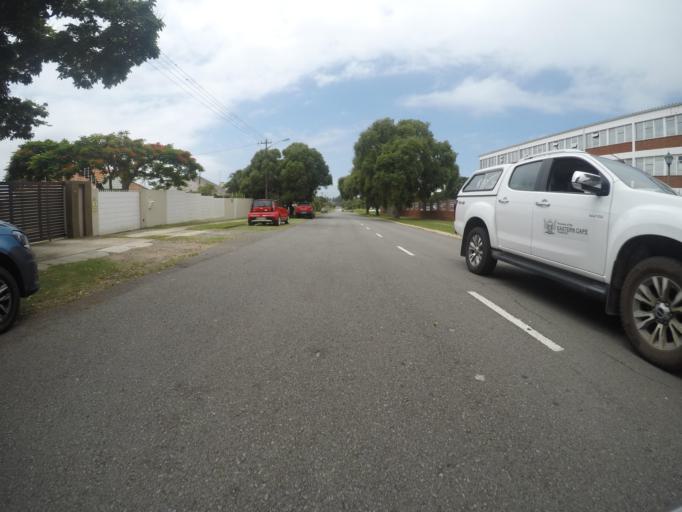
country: ZA
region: Eastern Cape
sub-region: Buffalo City Metropolitan Municipality
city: East London
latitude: -32.9922
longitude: 27.9262
